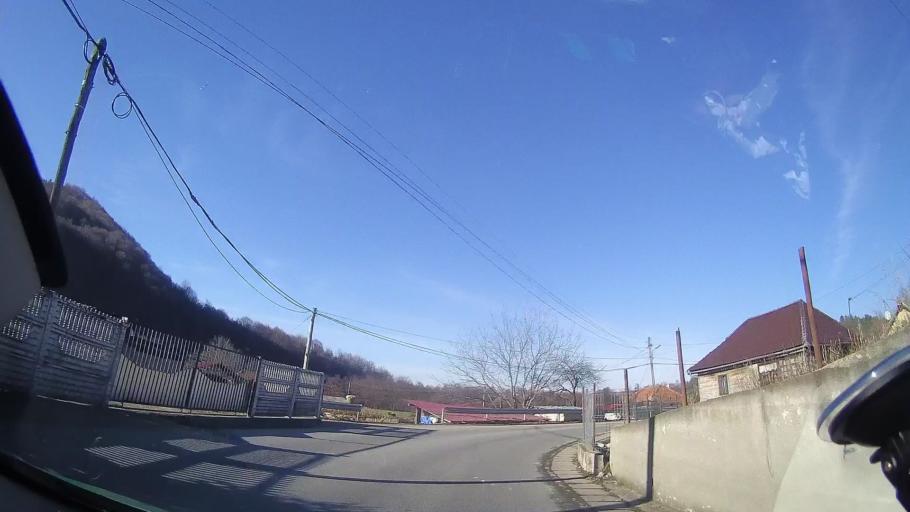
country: RO
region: Bihor
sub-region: Comuna Bratca
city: Bratca
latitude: 46.9204
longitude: 22.6204
